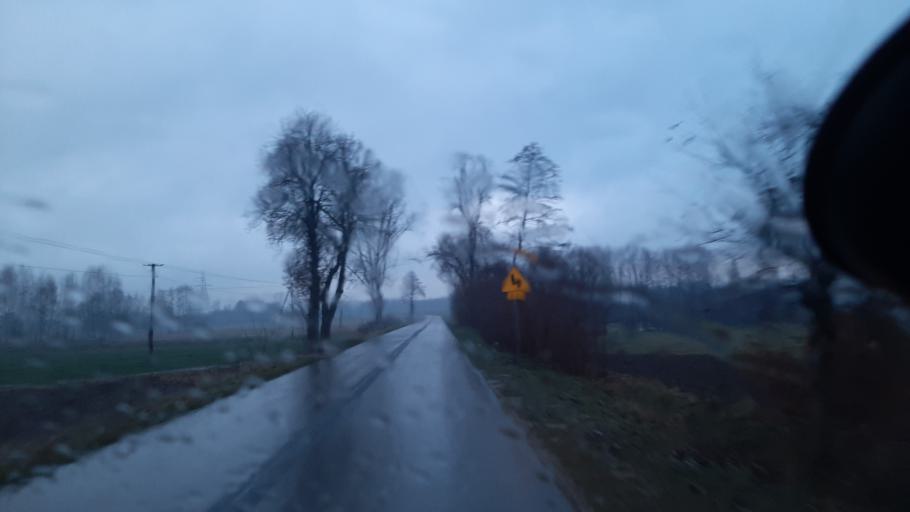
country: PL
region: Lublin Voivodeship
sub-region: Powiat lubartowski
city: Firlej
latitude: 51.5504
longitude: 22.5532
